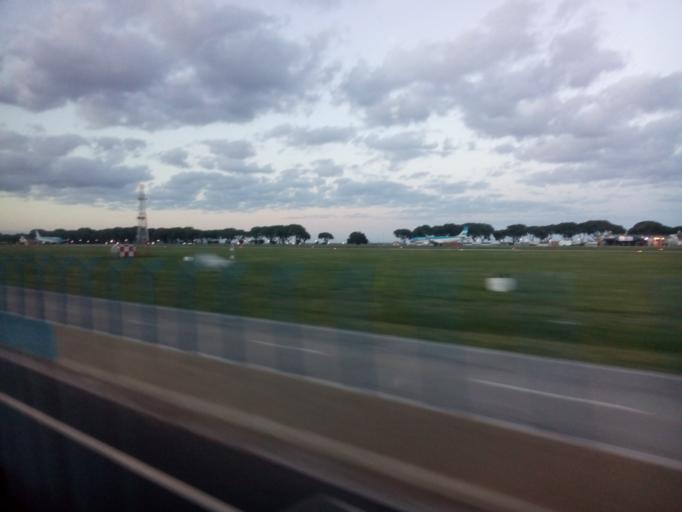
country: AR
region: Buenos Aires F.D.
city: Colegiales
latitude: -34.5576
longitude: -58.4229
